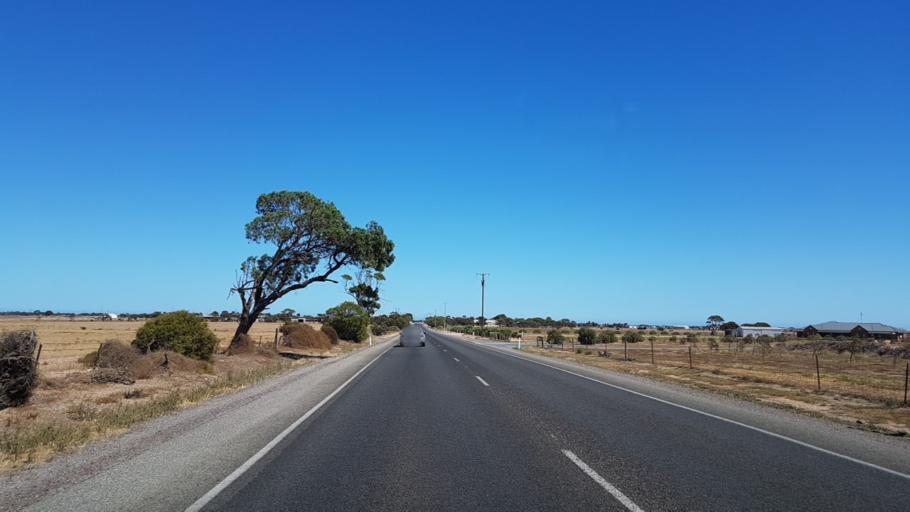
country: AU
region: South Australia
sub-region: Copper Coast
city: Wallaroo
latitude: -33.9447
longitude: 137.6619
